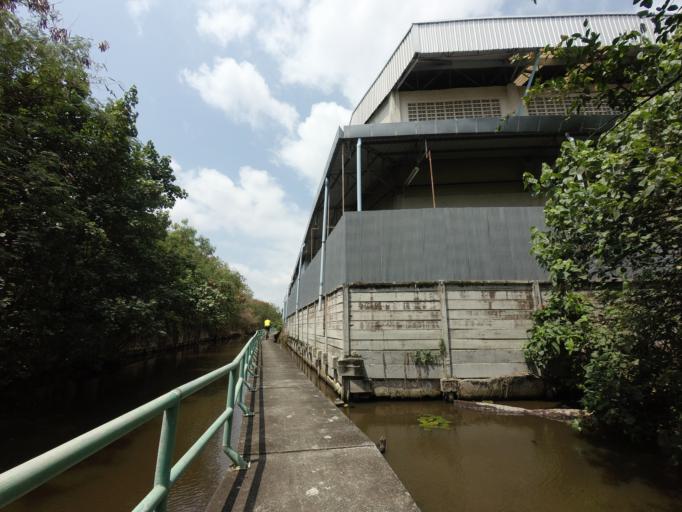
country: TH
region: Bangkok
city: Thung Khru
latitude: 13.6353
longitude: 100.4796
